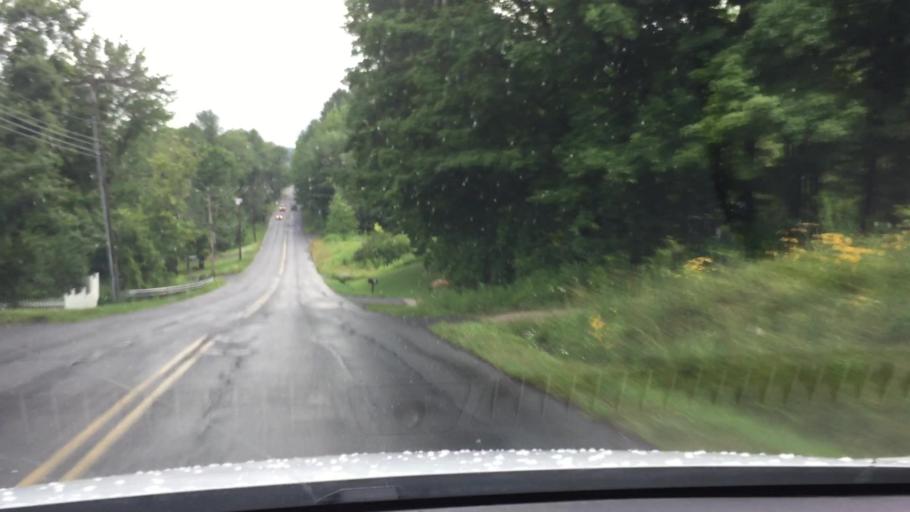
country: US
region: Massachusetts
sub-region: Berkshire County
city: Dalton
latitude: 42.4376
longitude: -73.1951
